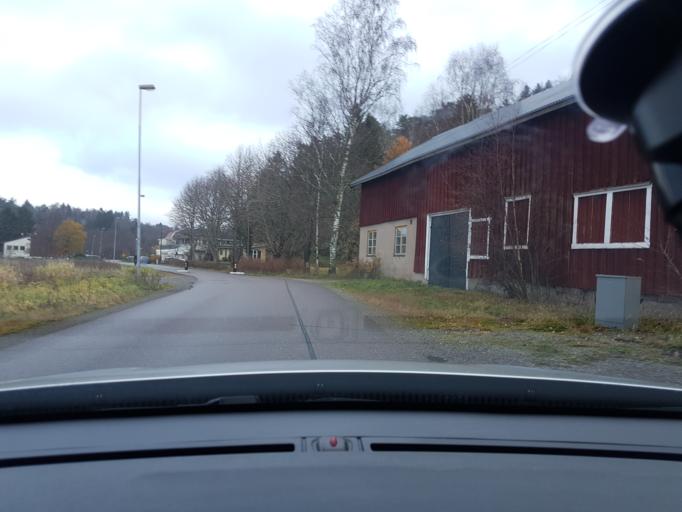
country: SE
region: Vaestra Goetaland
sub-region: Ale Kommun
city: Alafors
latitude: 57.9210
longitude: 12.0736
